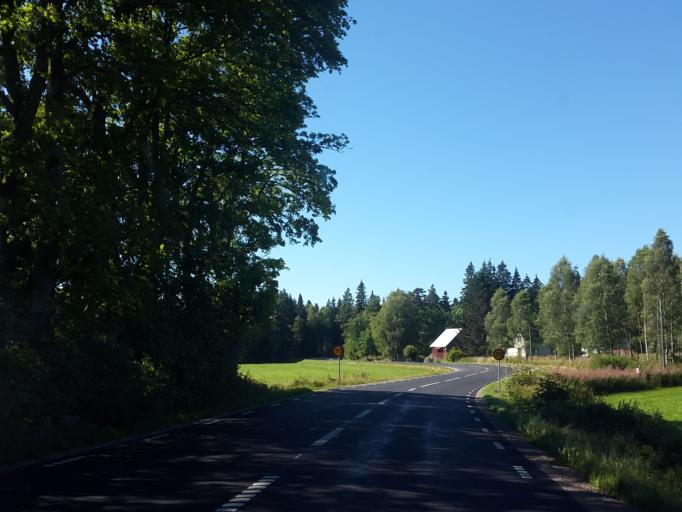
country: SE
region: Vaestra Goetaland
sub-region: Herrljunga Kommun
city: Herrljunga
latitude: 58.0135
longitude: 13.0466
